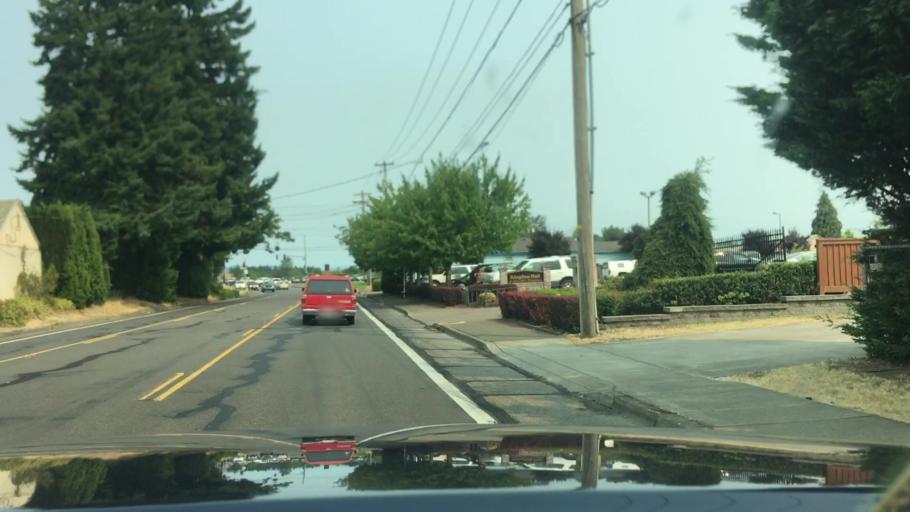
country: US
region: Oregon
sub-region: Lane County
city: Eugene
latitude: 44.0844
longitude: -123.1573
